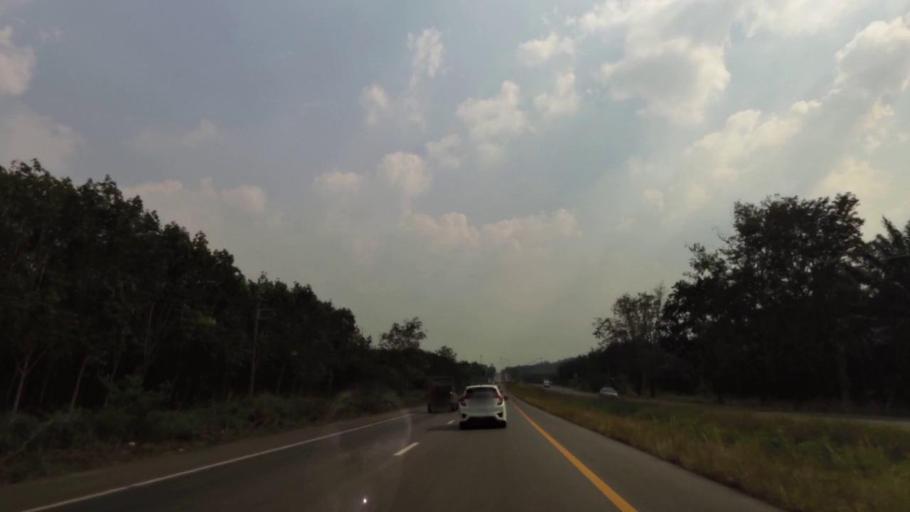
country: TH
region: Chon Buri
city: Nong Yai
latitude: 13.1085
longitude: 101.3783
